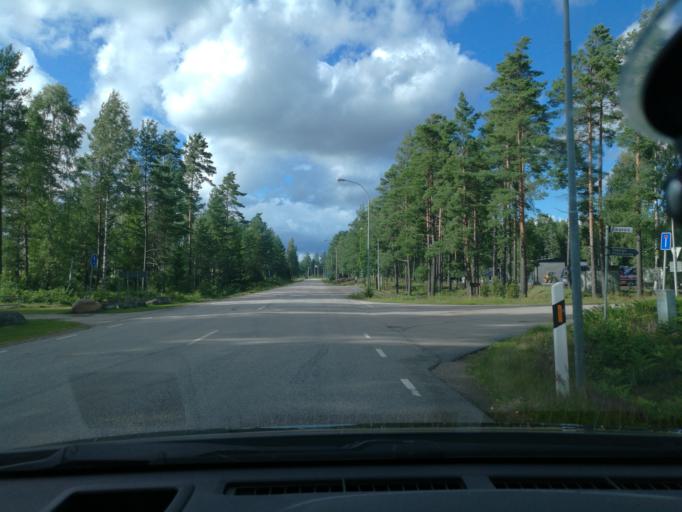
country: SE
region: Kronoberg
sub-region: Vaxjo Kommun
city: Braas
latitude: 57.0561
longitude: 15.0593
